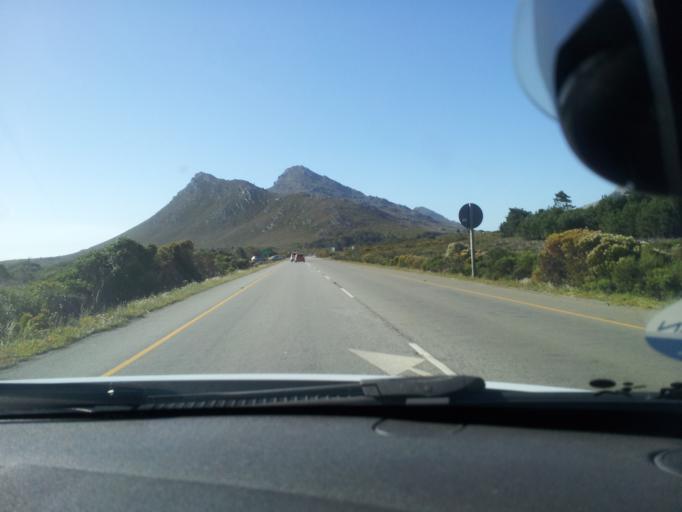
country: ZA
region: Western Cape
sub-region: Overberg District Municipality
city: Grabouw
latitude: -34.3415
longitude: 18.8454
